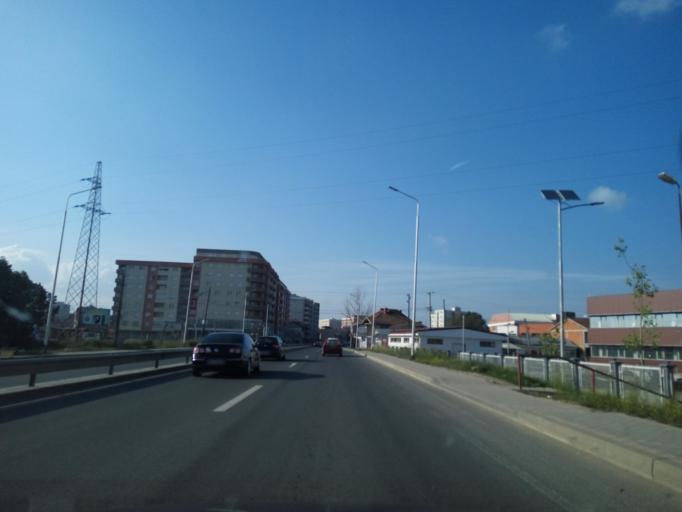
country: XK
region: Pristina
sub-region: Kosovo Polje
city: Kosovo Polje
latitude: 42.6321
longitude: 21.0918
